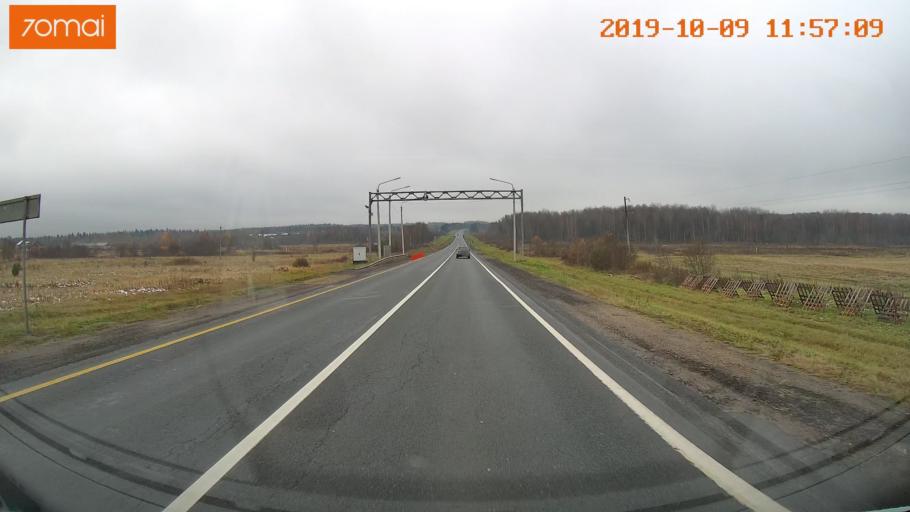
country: RU
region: Vologda
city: Gryazovets
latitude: 58.7359
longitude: 40.2910
